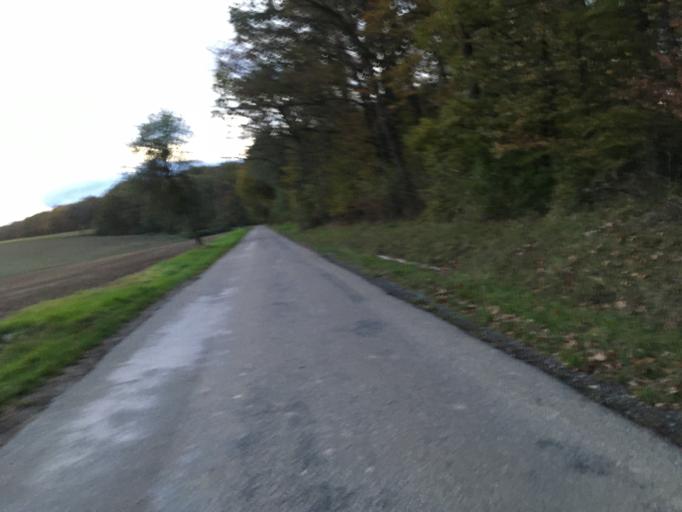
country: DE
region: Baden-Wuerttemberg
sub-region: Karlsruhe Region
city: Osterburken
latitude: 49.3921
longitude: 9.4581
